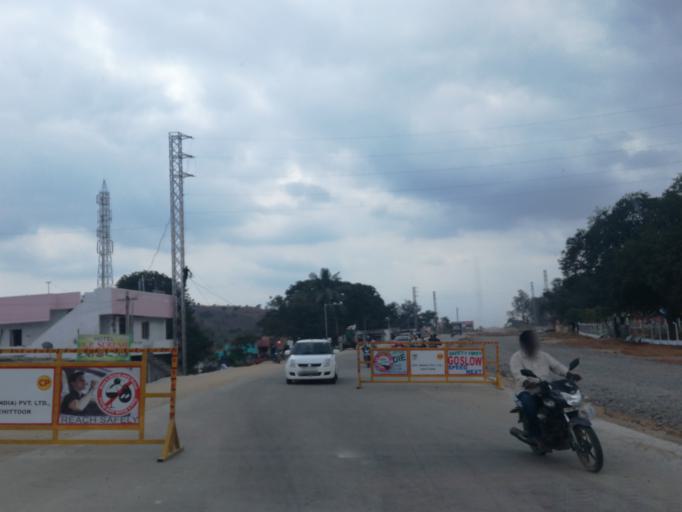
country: IN
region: Andhra Pradesh
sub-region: Chittoor
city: Ramapuram
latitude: 13.0935
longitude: 79.1333
